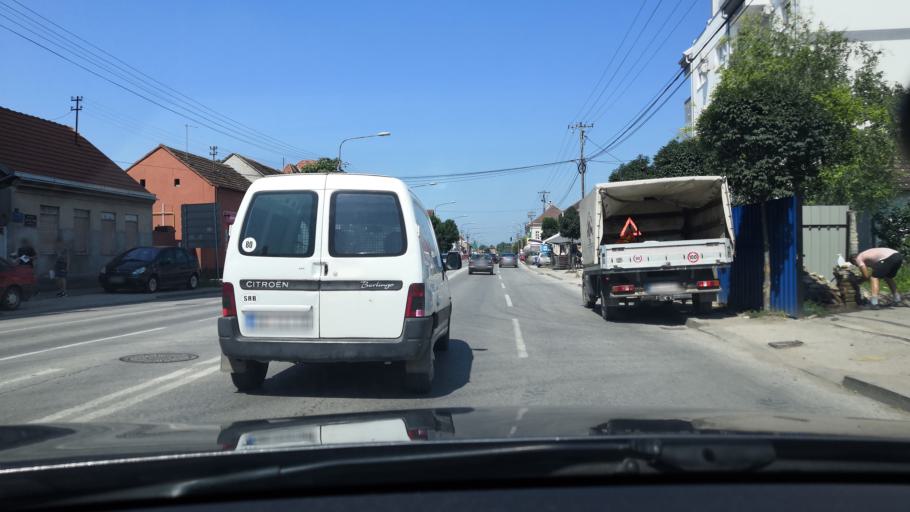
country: RS
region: Autonomna Pokrajina Vojvodina
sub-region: Sremski Okrug
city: Sremska Mitrovica
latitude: 44.9724
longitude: 19.6093
